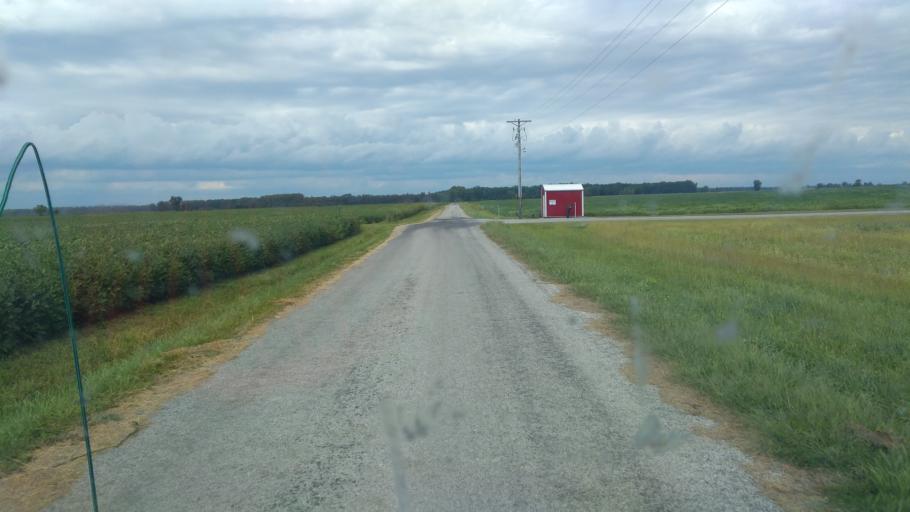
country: US
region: Ohio
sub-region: Wyandot County
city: Upper Sandusky
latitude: 40.6944
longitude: -83.2654
